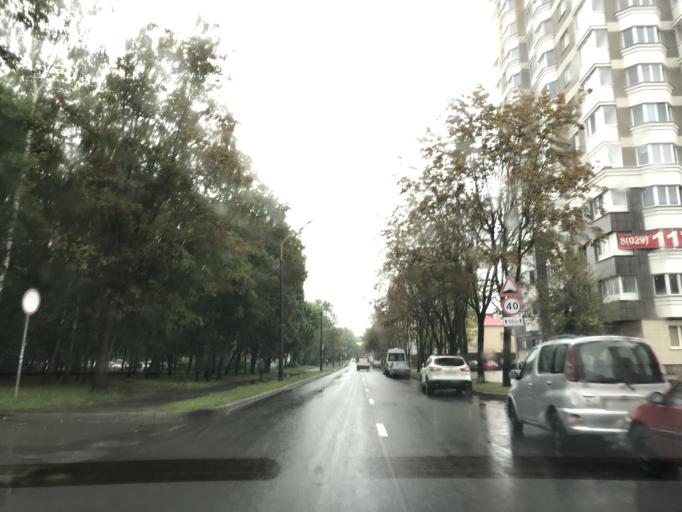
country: BY
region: Minsk
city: Bal'shavik
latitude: 53.9524
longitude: 27.6076
